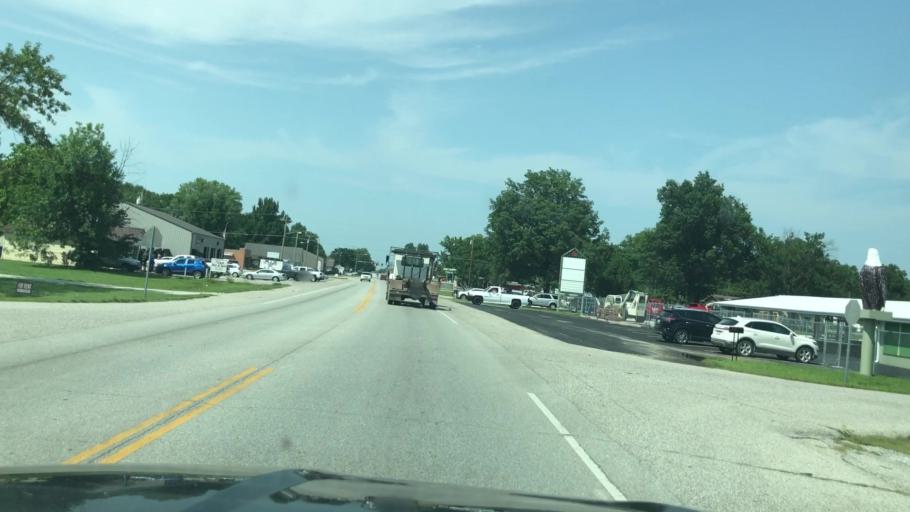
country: US
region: Oklahoma
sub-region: Ottawa County
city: Commerce
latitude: 36.9298
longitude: -94.8674
